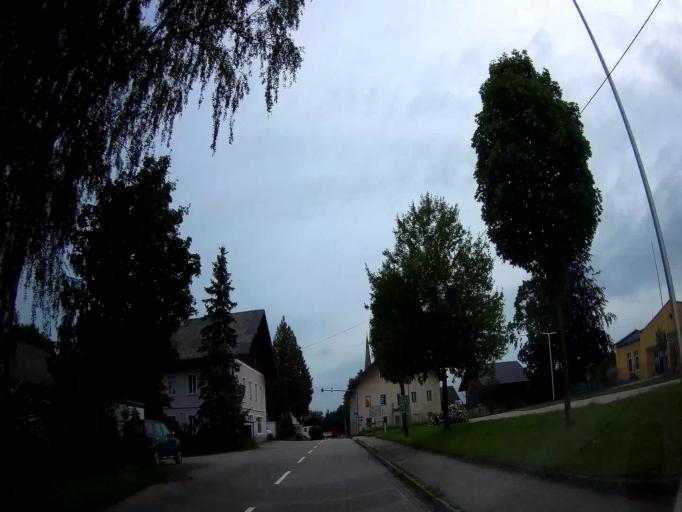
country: AT
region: Salzburg
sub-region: Politischer Bezirk Salzburg-Umgebung
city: Mattsee
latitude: 48.0145
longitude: 13.1270
